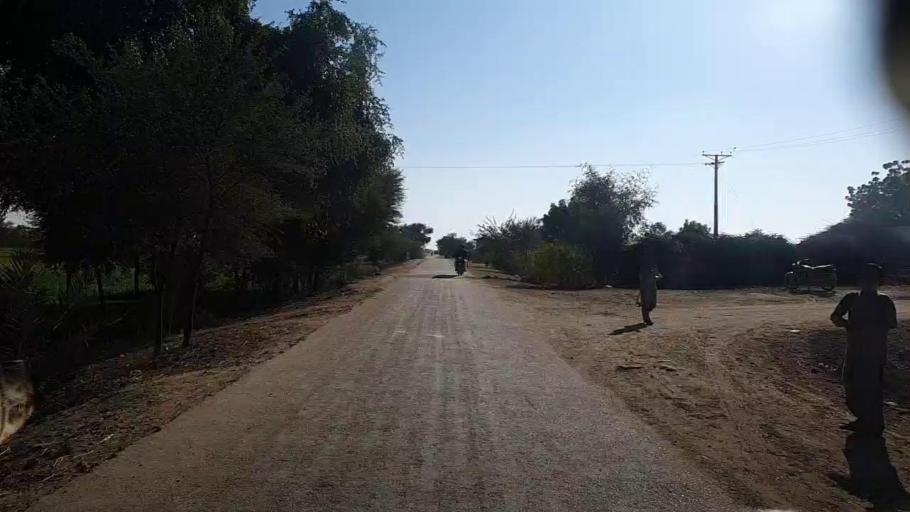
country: PK
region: Sindh
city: Khairpur
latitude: 27.9105
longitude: 69.7509
